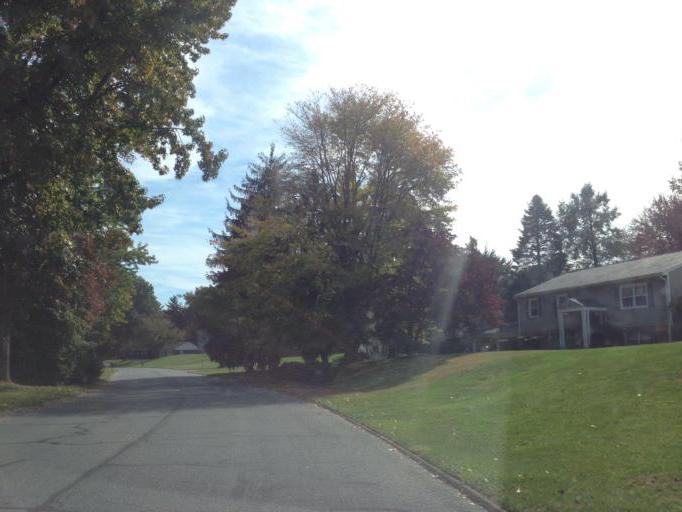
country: US
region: Maryland
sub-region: Howard County
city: Ellicott City
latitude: 39.2858
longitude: -76.8369
